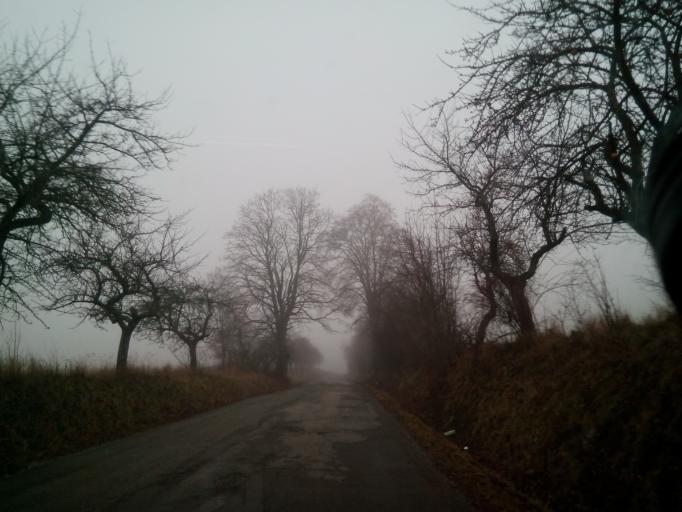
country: SK
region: Presovsky
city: Spisske Podhradie
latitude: 49.0297
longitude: 20.7977
